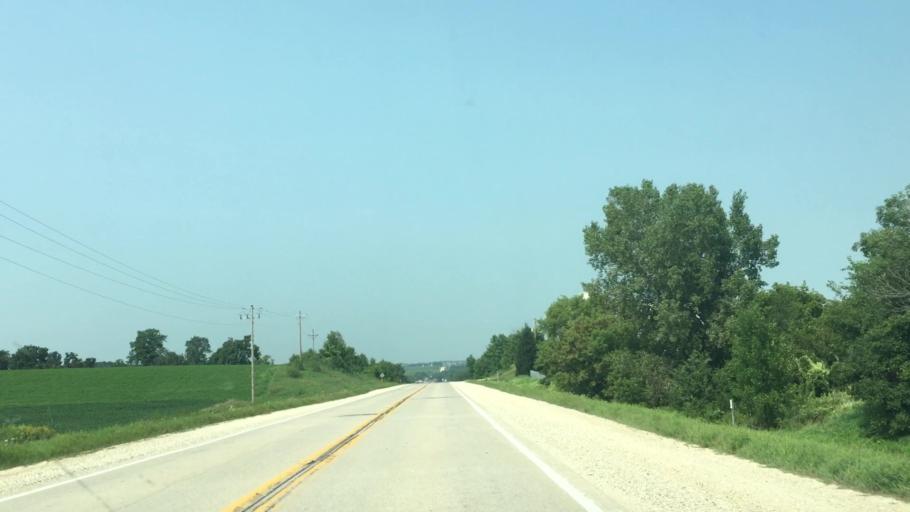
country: US
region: Iowa
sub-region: Fayette County
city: West Union
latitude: 43.1018
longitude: -91.8691
